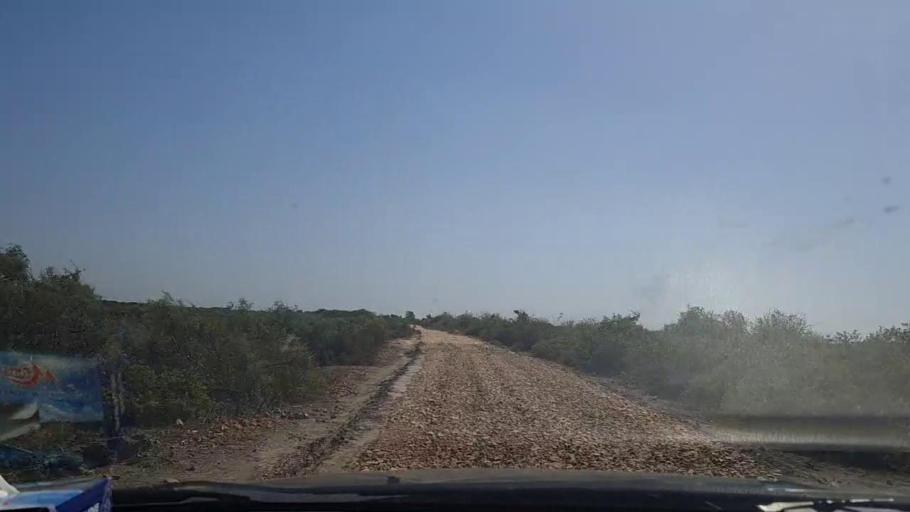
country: PK
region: Sindh
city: Chuhar Jamali
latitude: 24.2721
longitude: 67.7460
